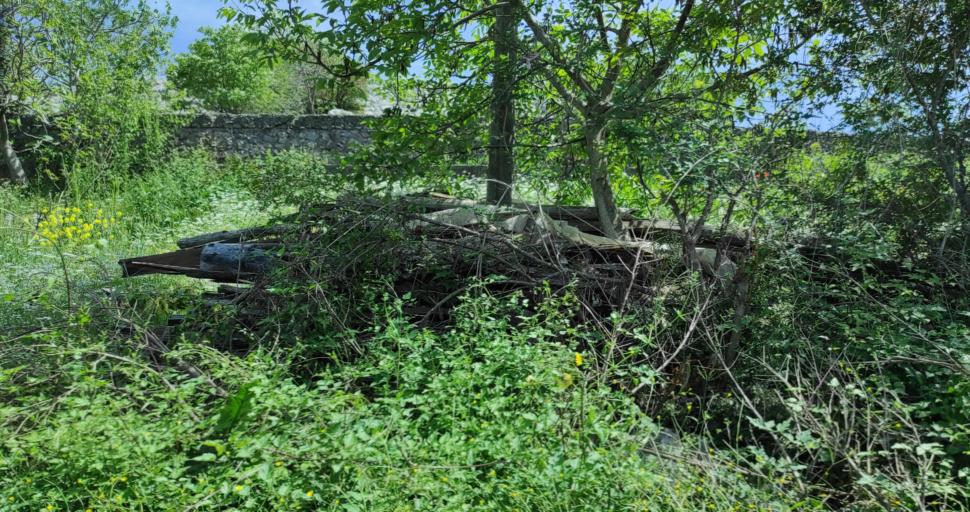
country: AL
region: Shkoder
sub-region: Rrethi i Malesia e Madhe
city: Gruemire
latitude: 42.1335
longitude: 19.5511
